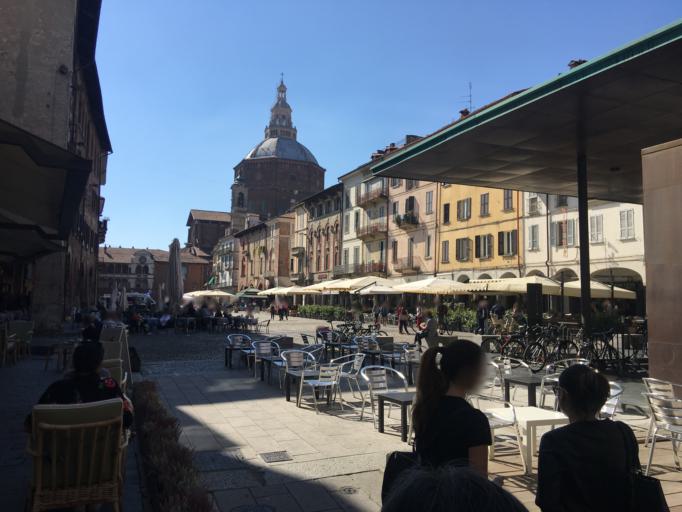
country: IT
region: Lombardy
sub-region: Provincia di Pavia
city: Pavia
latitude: 45.1863
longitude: 9.1549
